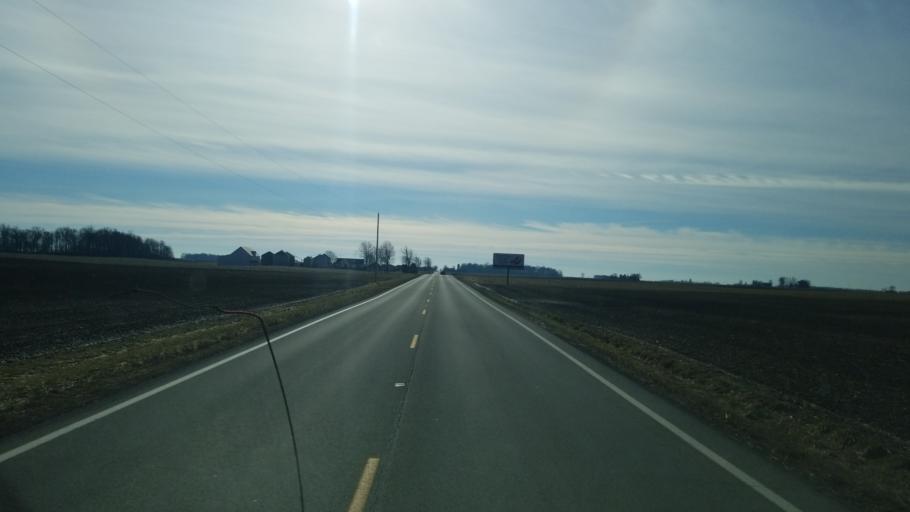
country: US
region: Ohio
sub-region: Putnam County
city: Leipsic
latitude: 41.0796
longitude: -83.9865
